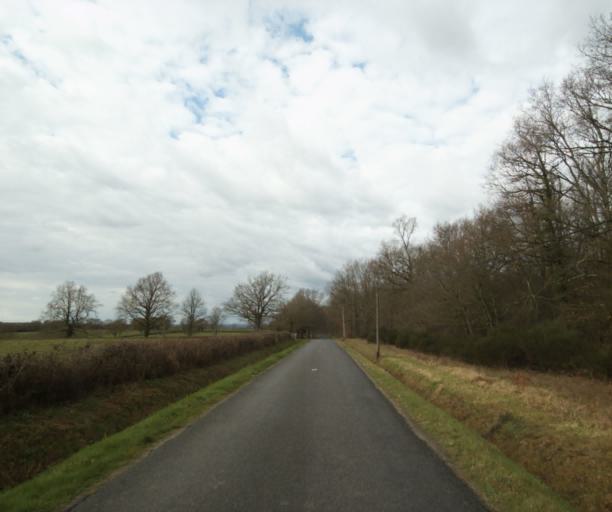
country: FR
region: Auvergne
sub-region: Departement de l'Allier
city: Toulon-sur-Allier
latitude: 46.5283
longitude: 3.4056
